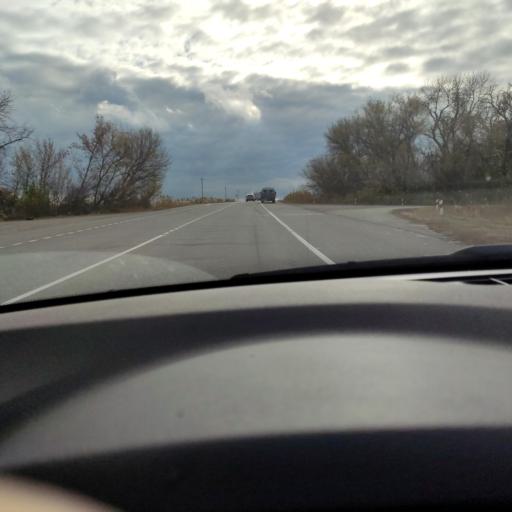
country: RU
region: Voronezj
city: Devitsa
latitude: 51.5720
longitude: 38.9747
